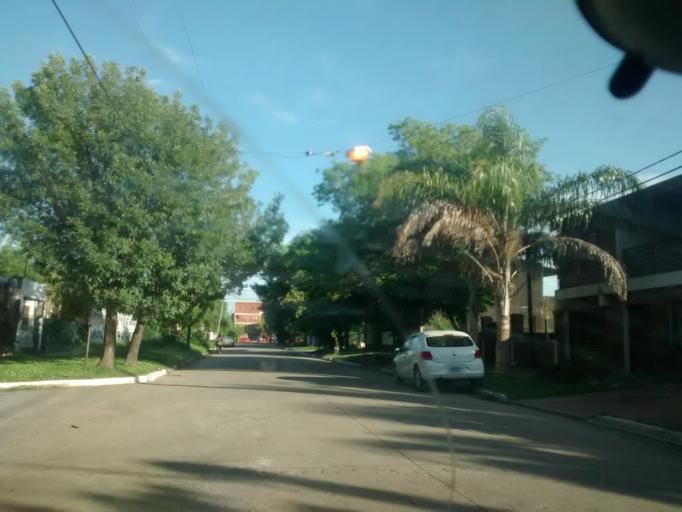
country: AR
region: Chaco
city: Resistencia
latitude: -27.4637
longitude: -58.9977
